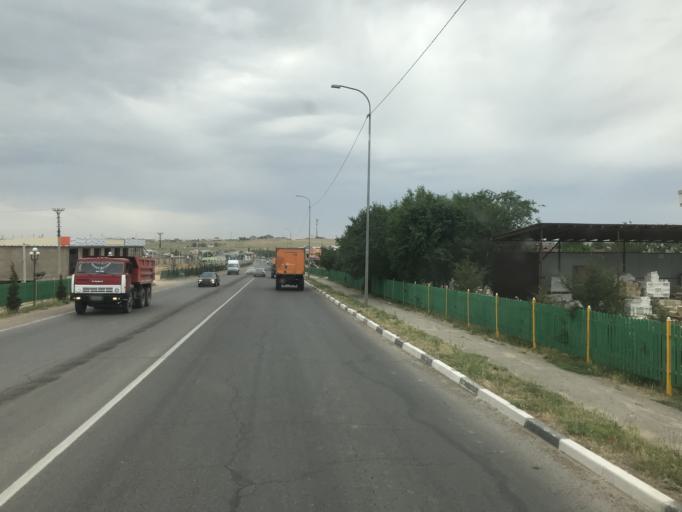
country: KZ
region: Ongtustik Qazaqstan
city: Saryaghash
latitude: 41.4730
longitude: 69.1896
